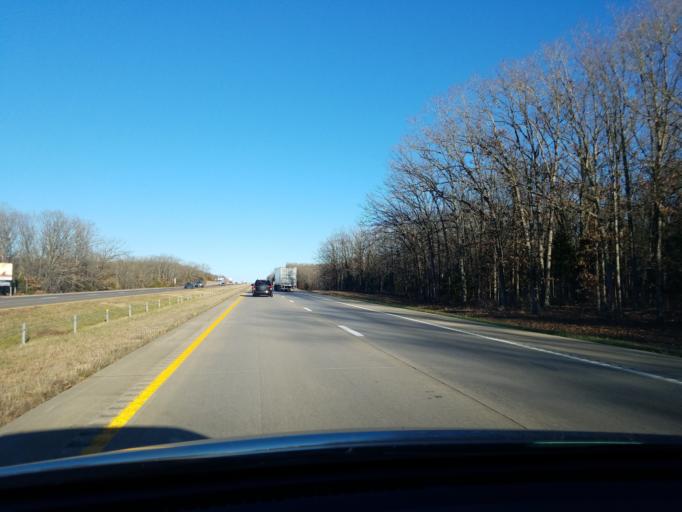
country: US
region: Missouri
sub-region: Crawford County
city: Cuba
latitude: 38.0583
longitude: -91.4377
